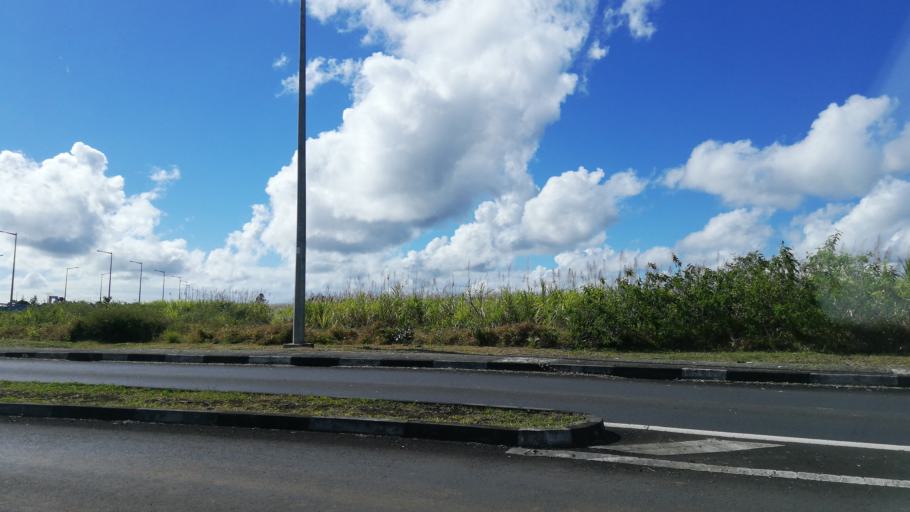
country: MU
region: Moka
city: Quartier Militaire
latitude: -20.2554
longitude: 57.5736
